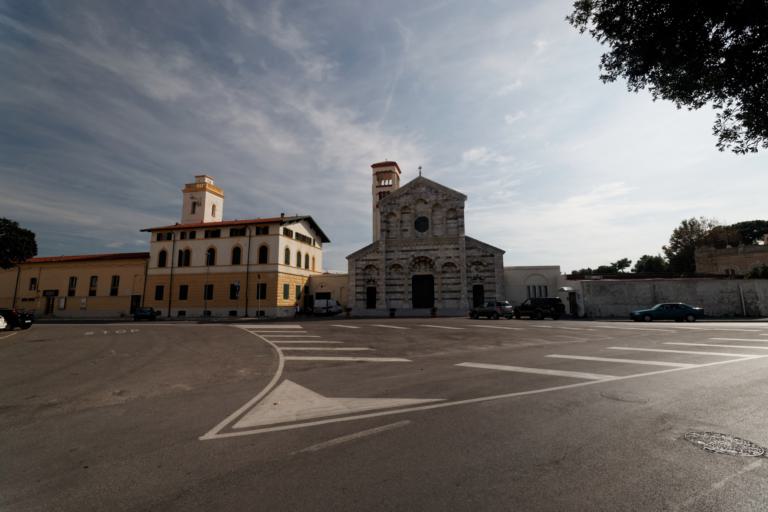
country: IT
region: Tuscany
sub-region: Province of Pisa
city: Marina di Pisa
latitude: 43.6740
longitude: 10.2735
